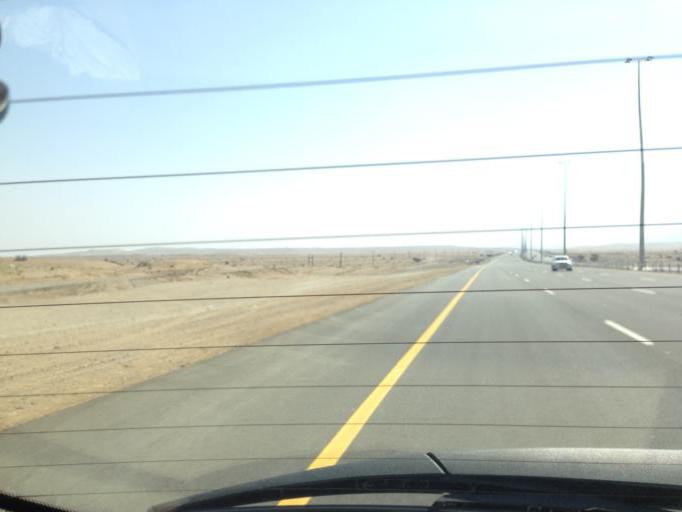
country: OM
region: Al Batinah
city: Rustaq
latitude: 23.5287
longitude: 57.5959
